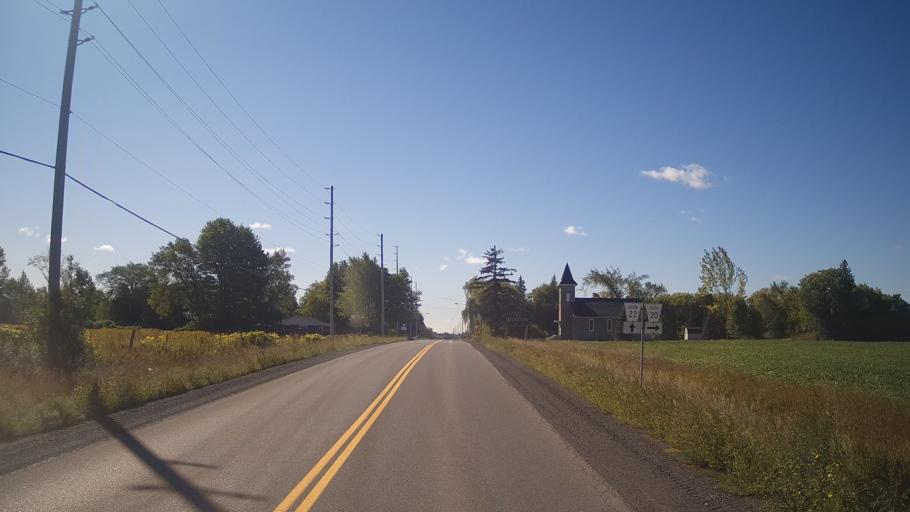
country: CA
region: Ontario
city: Prescott
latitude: 44.9713
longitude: -75.5332
